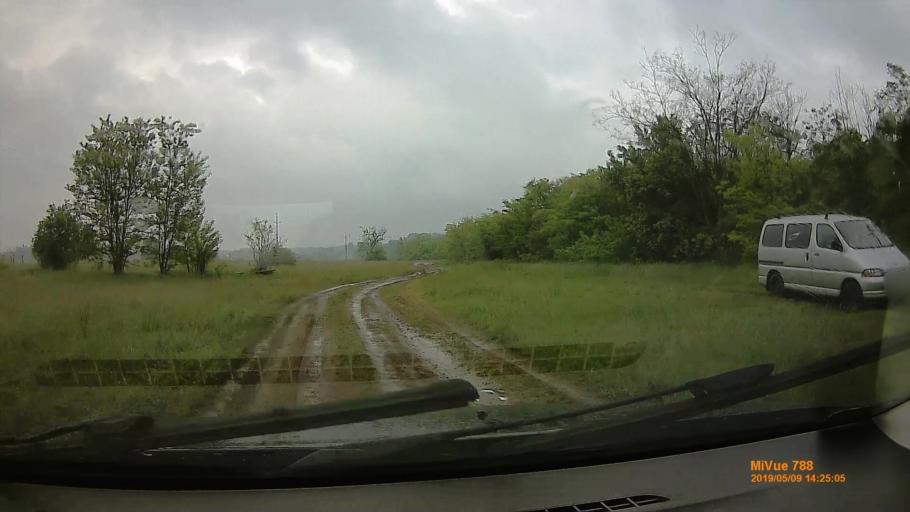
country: HU
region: Budapest
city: Budapest XVII. keruelet
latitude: 47.4982
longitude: 19.2143
